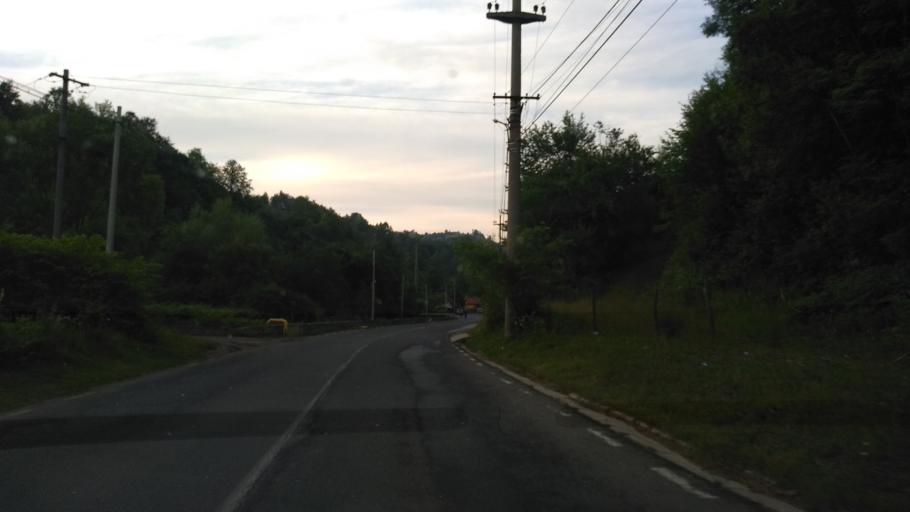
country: RO
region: Hunedoara
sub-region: Comuna Aninoasa
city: Aninoasa
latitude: 45.3955
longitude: 23.3184
